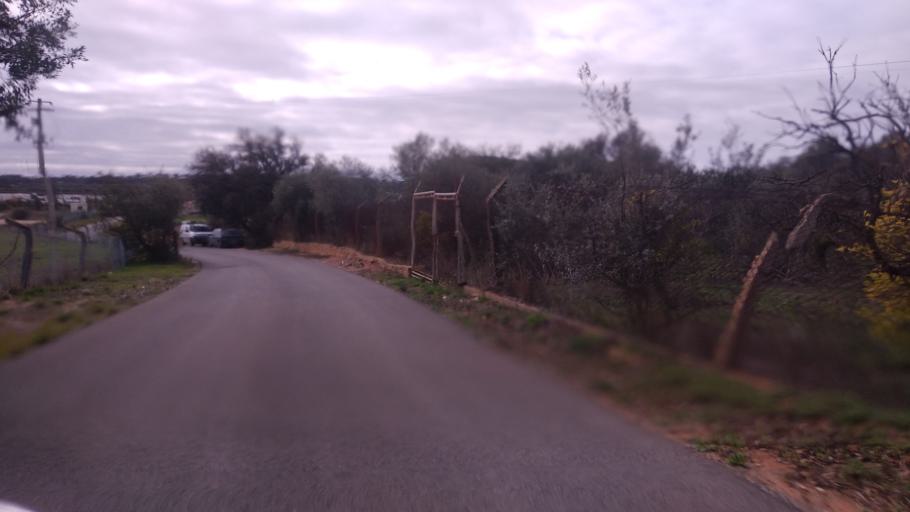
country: PT
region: Faro
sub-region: Faro
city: Santa Barbara de Nexe
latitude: 37.0689
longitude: -7.9723
